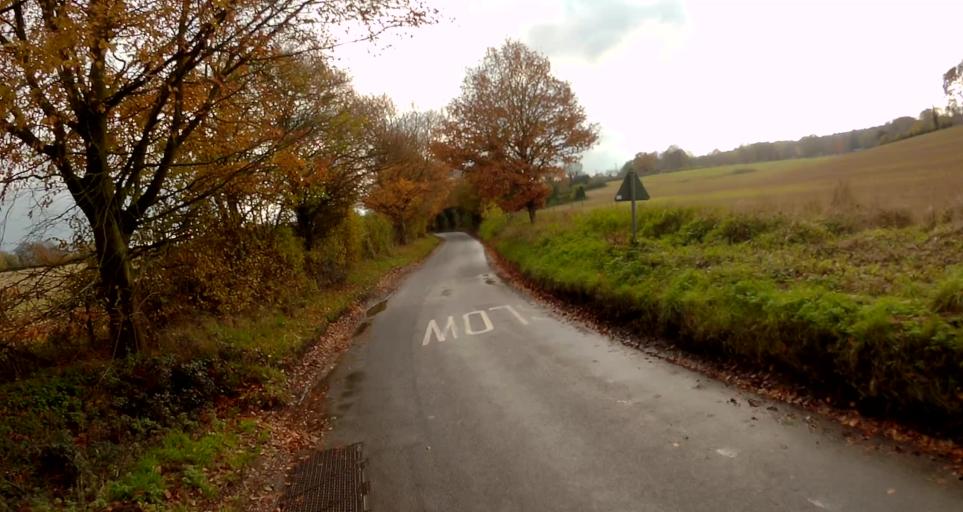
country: GB
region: England
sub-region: Hampshire
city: Old Basing
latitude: 51.2355
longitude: -1.0291
